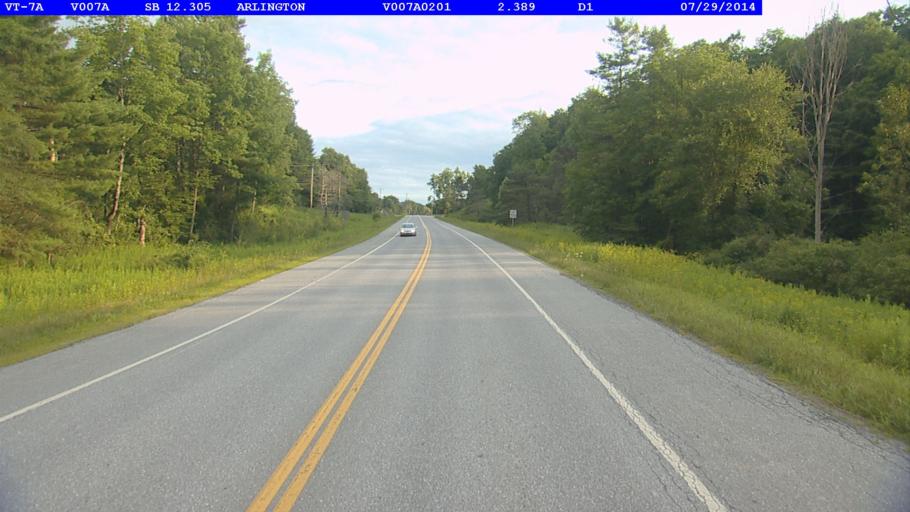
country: US
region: Vermont
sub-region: Bennington County
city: Arlington
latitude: 43.0544
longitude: -73.1633
